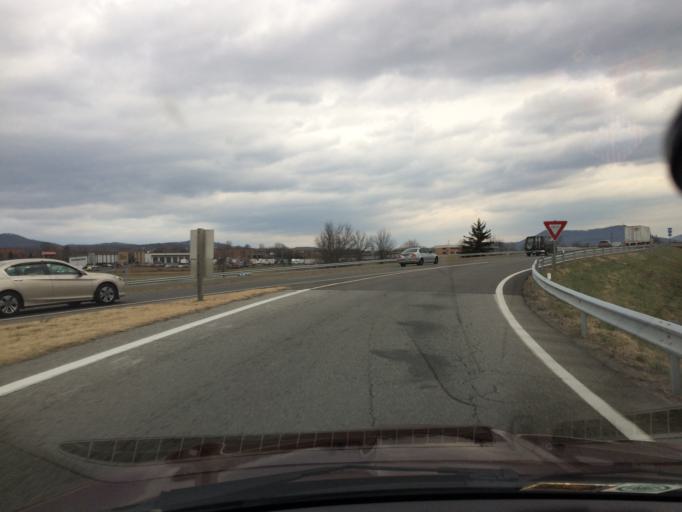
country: US
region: Virginia
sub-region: Roanoke County
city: Hollins
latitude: 37.3260
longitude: -79.9903
